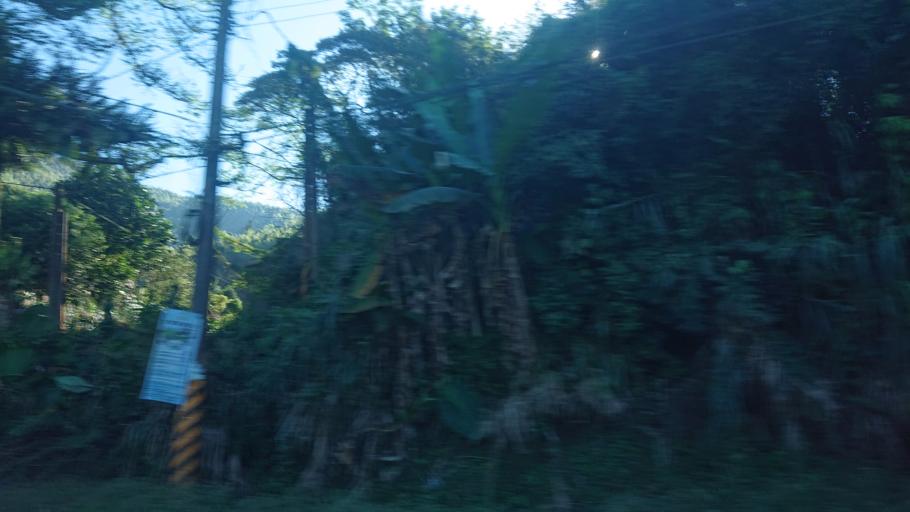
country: TW
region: Taiwan
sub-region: Chiayi
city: Jiayi Shi
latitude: 23.5239
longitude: 120.6323
